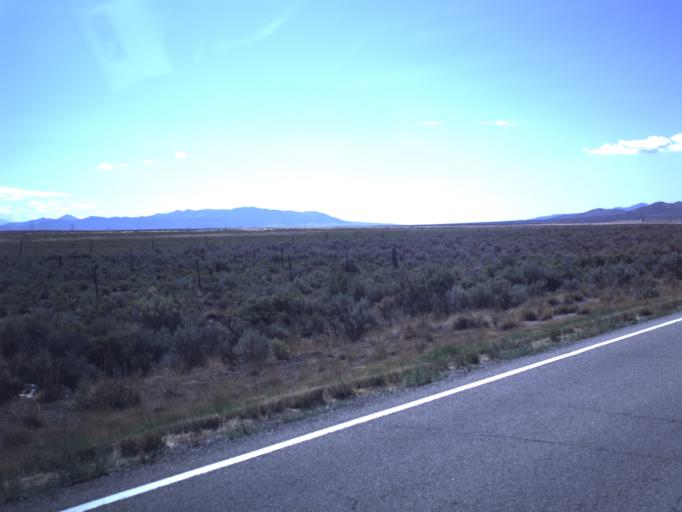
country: US
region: Utah
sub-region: Tooele County
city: Tooele
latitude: 40.2314
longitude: -112.4032
